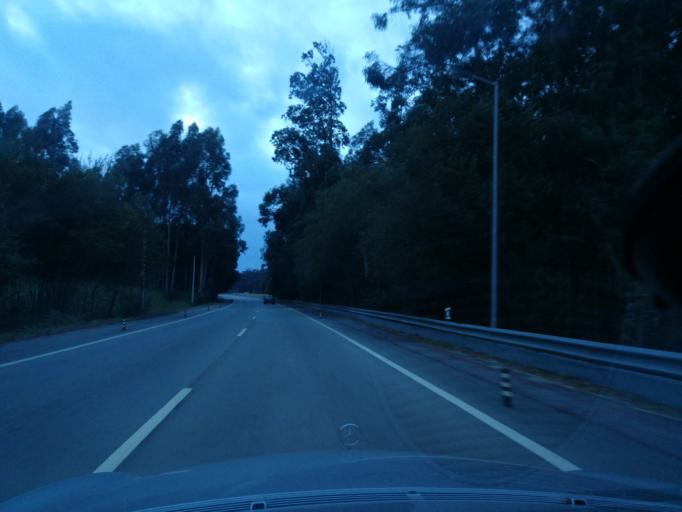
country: PT
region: Aveiro
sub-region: Murtosa
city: Murtosa
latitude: 40.7612
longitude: -8.6148
